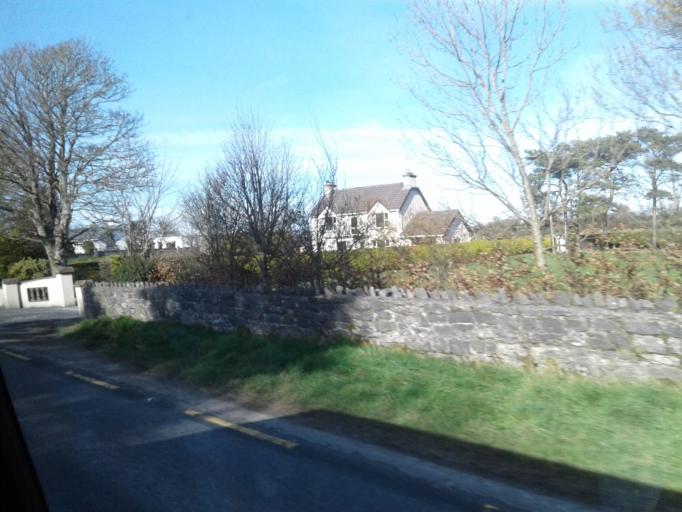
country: IE
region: Connaught
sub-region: County Galway
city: Oranmore
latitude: 53.1864
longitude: -8.8474
